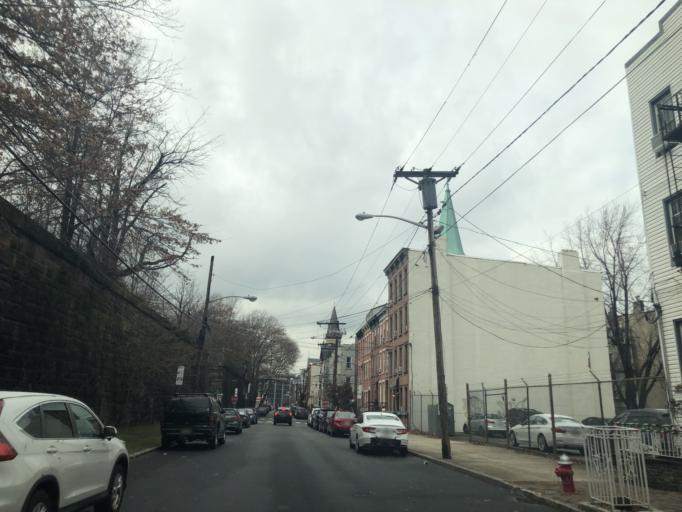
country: US
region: New Jersey
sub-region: Hudson County
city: Hoboken
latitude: 40.7257
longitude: -74.0477
